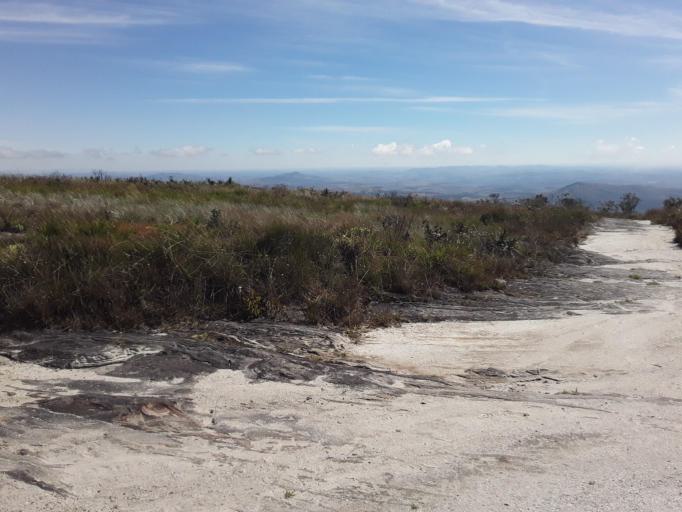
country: BR
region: Minas Gerais
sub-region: Lima Duarte
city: Lima Duarte
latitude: -21.6835
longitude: -43.8873
